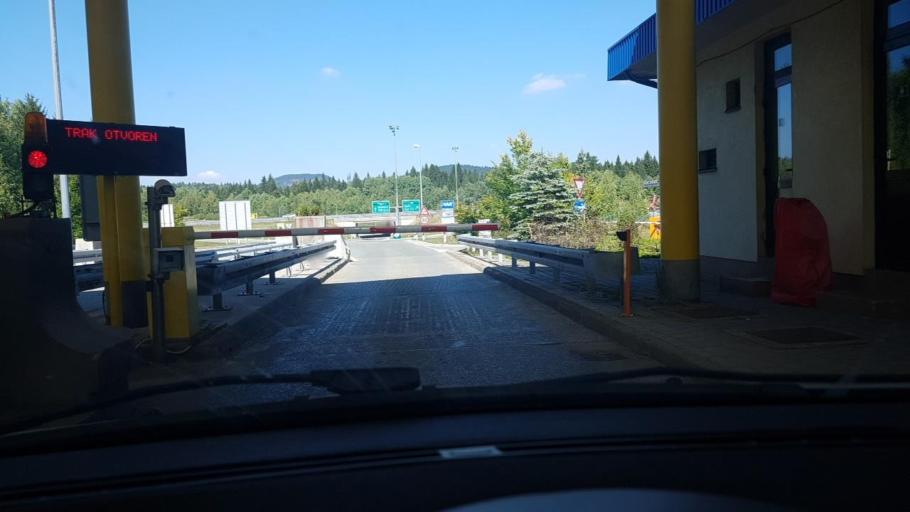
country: HR
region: Primorsko-Goranska
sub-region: Grad Delnice
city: Delnice
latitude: 45.3820
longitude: 14.9128
